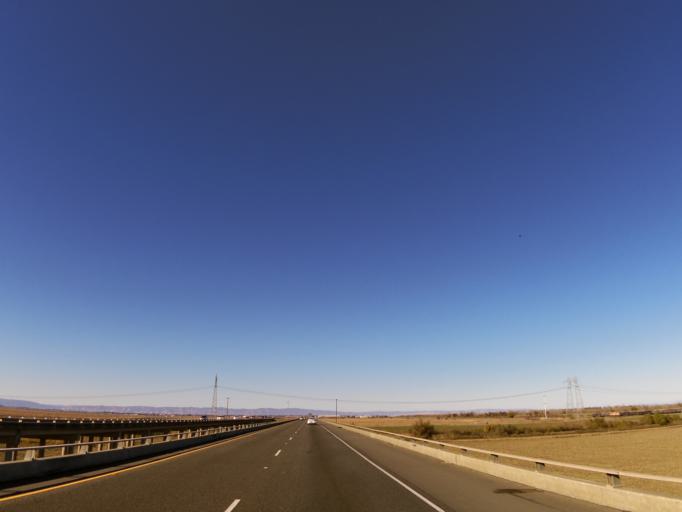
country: US
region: California
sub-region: Yolo County
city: Woodland
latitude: 38.6737
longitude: -121.6685
